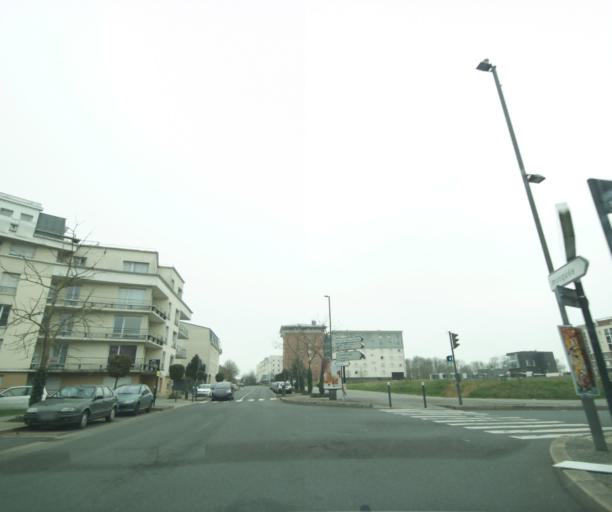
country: FR
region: Ile-de-France
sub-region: Departement du Val-d'Oise
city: Courdimanche
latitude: 49.0462
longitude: 2.0125
